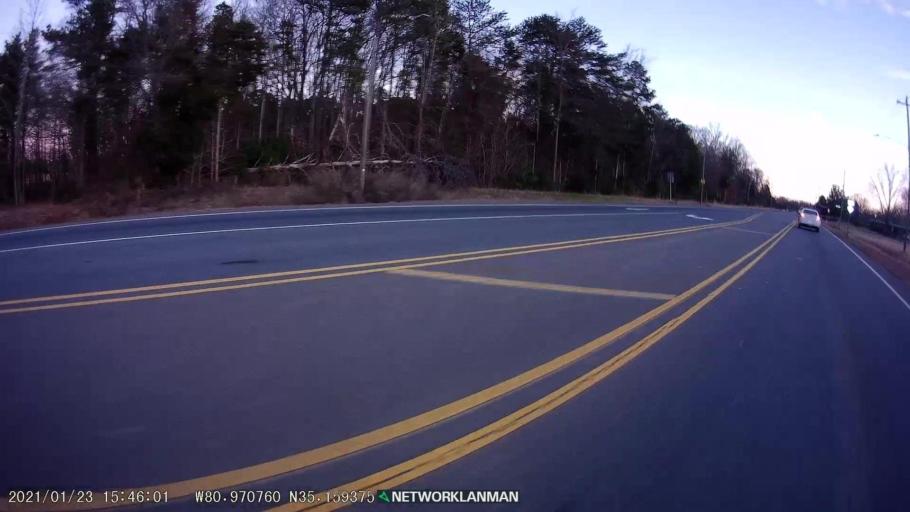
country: US
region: South Carolina
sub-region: York County
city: Lake Wylie
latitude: 35.1592
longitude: -80.9707
